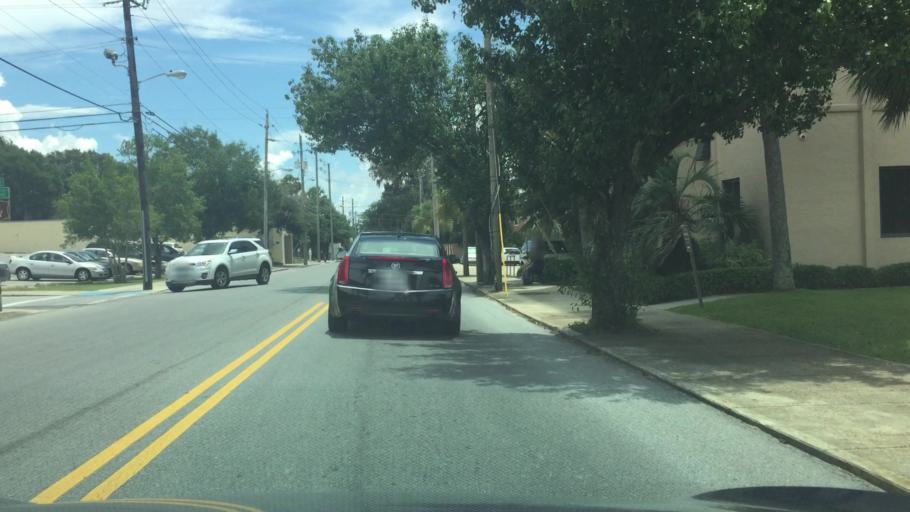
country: US
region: Florida
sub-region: Bay County
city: Panama City
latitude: 30.1536
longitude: -85.6621
